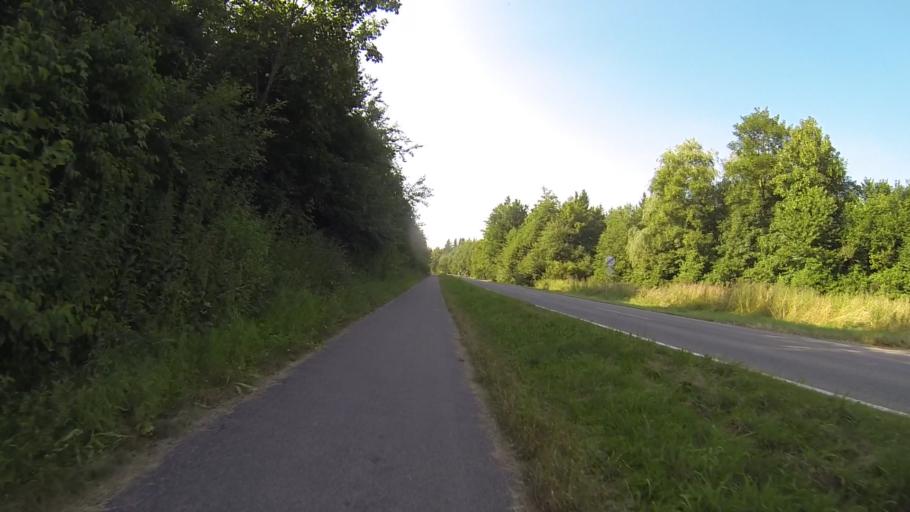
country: DE
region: Baden-Wuerttemberg
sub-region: Tuebingen Region
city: Staig
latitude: 48.3083
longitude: 9.9704
